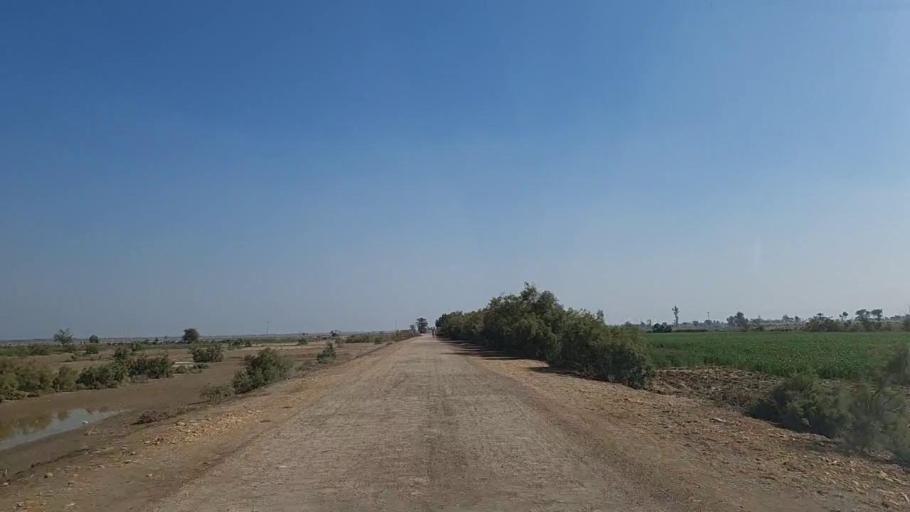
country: PK
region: Sindh
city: Nawabshah
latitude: 26.3415
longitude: 68.4352
